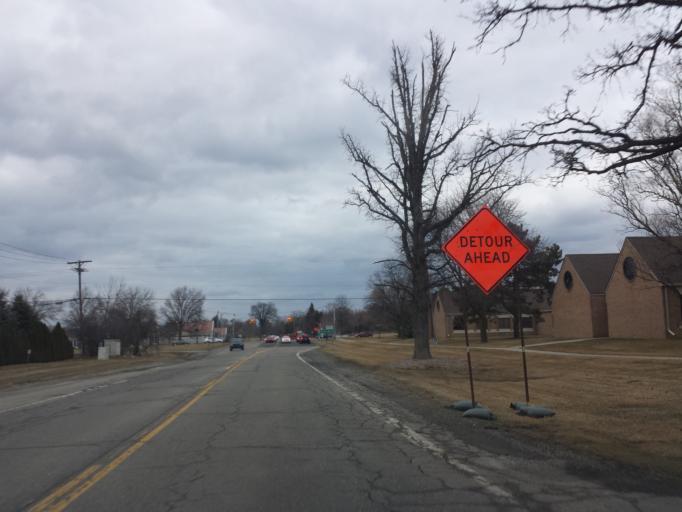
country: US
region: Michigan
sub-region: Oakland County
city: Beverly Hills
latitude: 42.5150
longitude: -83.2425
